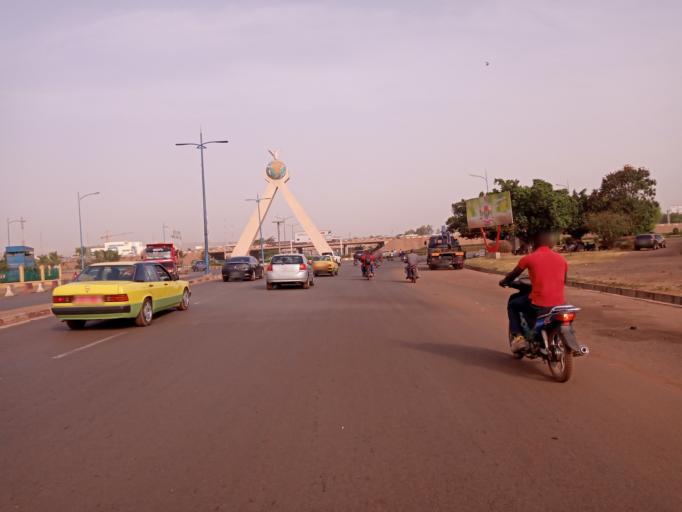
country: ML
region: Bamako
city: Bamako
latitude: 12.6307
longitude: -8.0099
